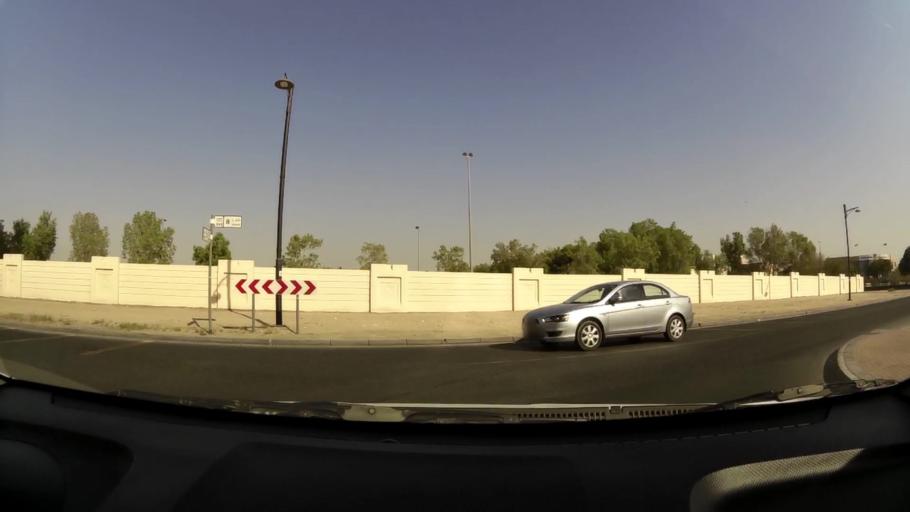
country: AE
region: Ash Shariqah
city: Sharjah
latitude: 25.2864
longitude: 55.3717
